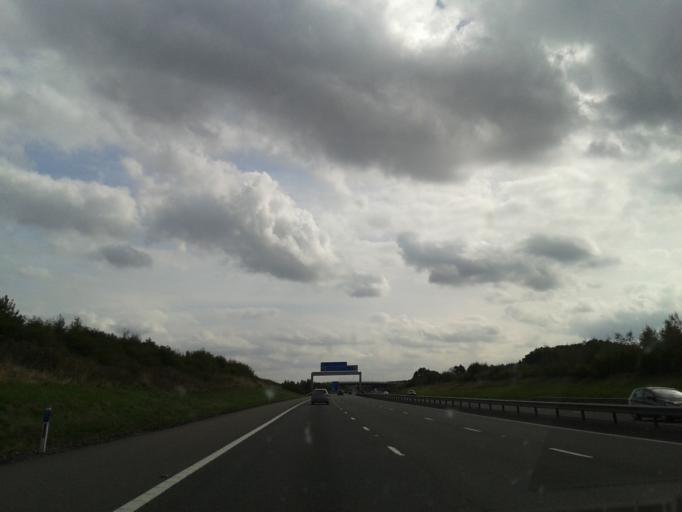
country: GB
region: England
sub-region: Staffordshire
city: Shenstone
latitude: 52.6445
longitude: -1.8240
